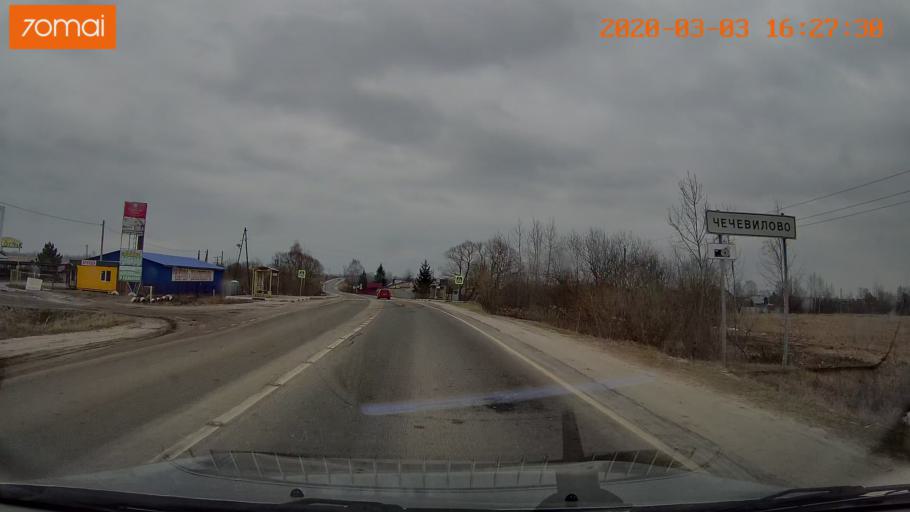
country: RU
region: Moskovskaya
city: Konobeyevo
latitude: 55.4364
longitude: 38.6731
